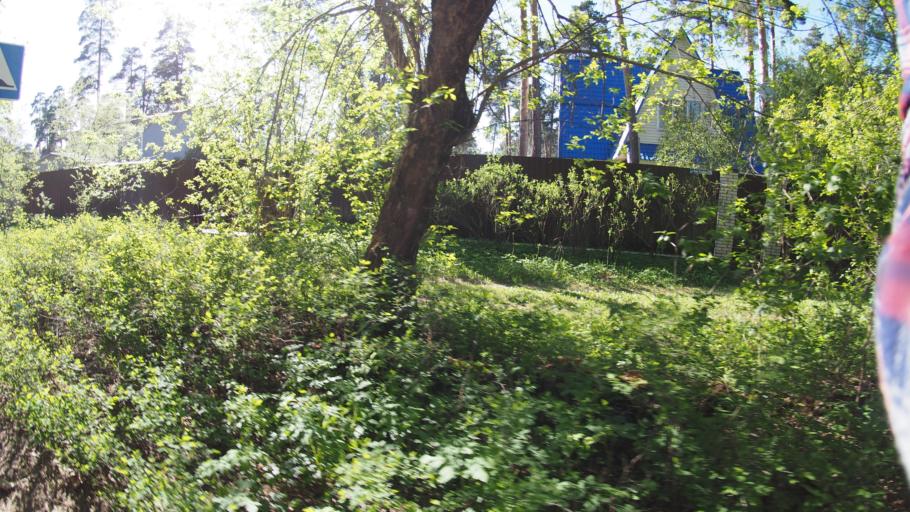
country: RU
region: Moskovskaya
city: Kratovo
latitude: 55.5754
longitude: 38.1811
